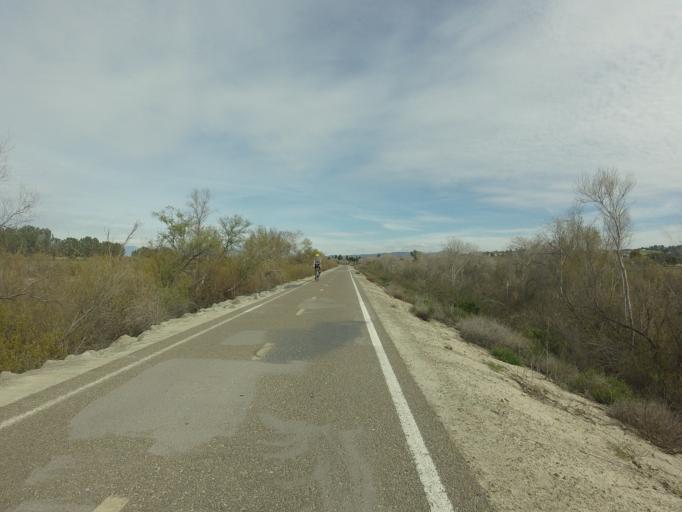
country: US
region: California
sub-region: San Diego County
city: Camp Pendleton South
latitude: 33.2399
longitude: -117.3123
